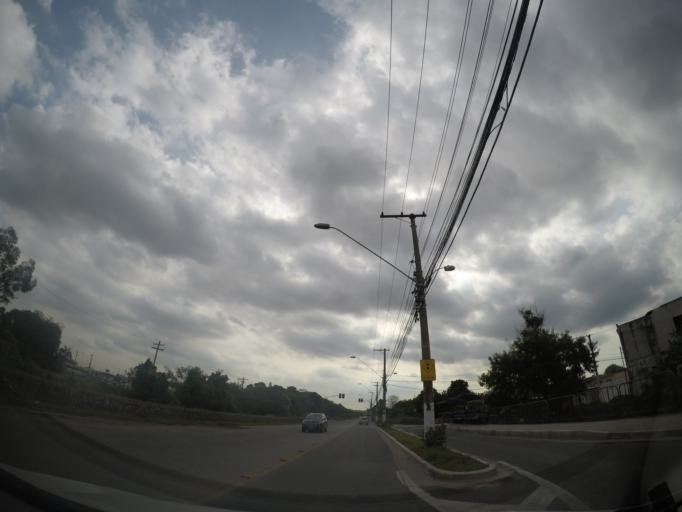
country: BR
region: Sao Paulo
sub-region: Guarulhos
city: Guarulhos
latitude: -23.4190
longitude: -46.4819
